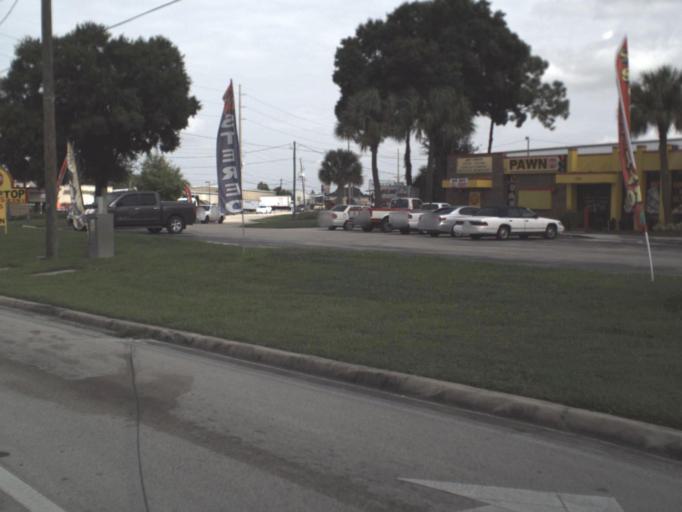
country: US
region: Florida
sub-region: Polk County
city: Jan-Phyl Village
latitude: 28.0255
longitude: -81.7757
